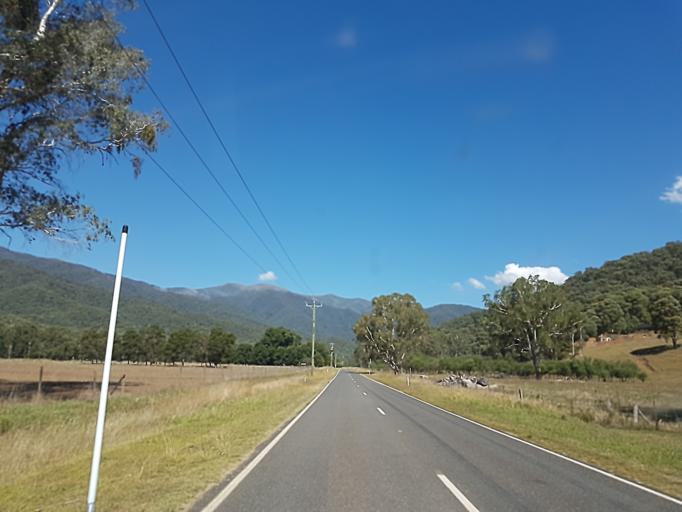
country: AU
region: Victoria
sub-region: Alpine
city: Mount Beauty
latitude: -36.8281
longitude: 147.0709
